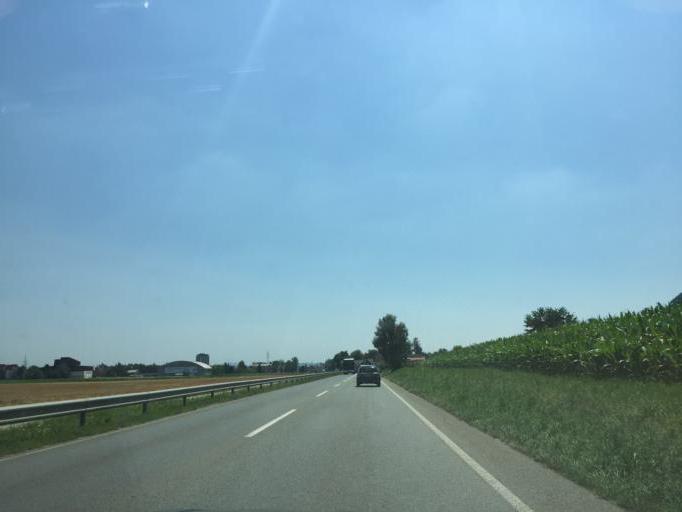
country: SI
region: Kranj
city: Kranj
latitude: 46.2542
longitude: 14.3419
